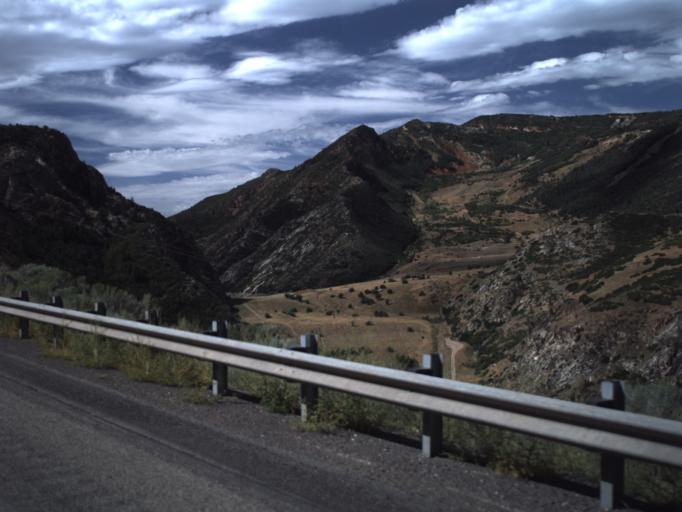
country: US
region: Utah
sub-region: Utah County
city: Mapleton
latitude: 40.0090
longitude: -111.4919
